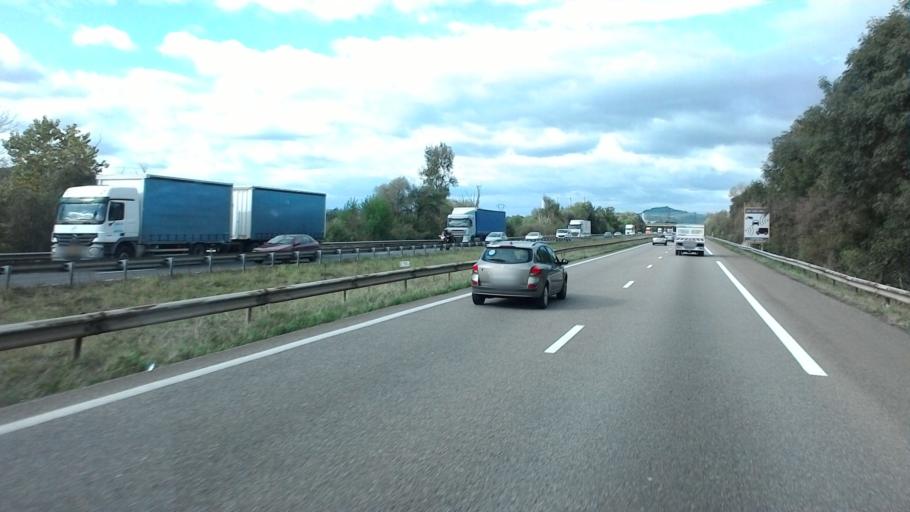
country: FR
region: Lorraine
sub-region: Departement de Meurthe-et-Moselle
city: Dieulouard
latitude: 48.8436
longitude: 6.0905
